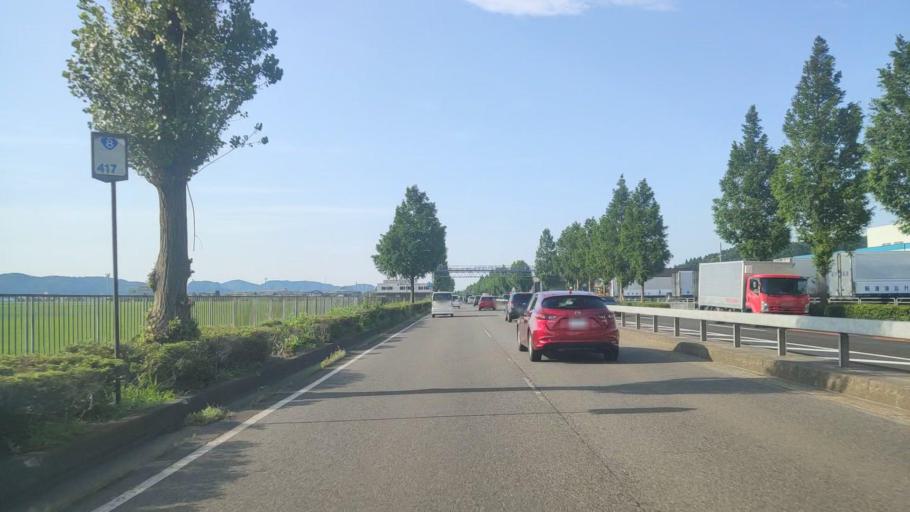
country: JP
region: Fukui
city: Sabae
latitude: 35.9973
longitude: 136.2063
